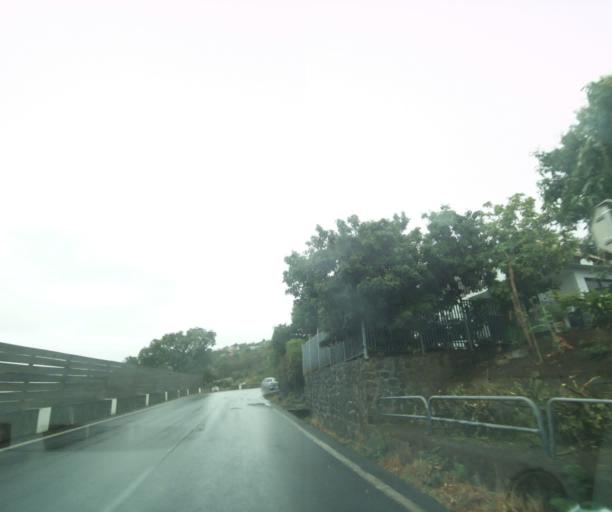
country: RE
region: Reunion
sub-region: Reunion
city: Saint-Paul
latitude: -21.0154
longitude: 55.2805
